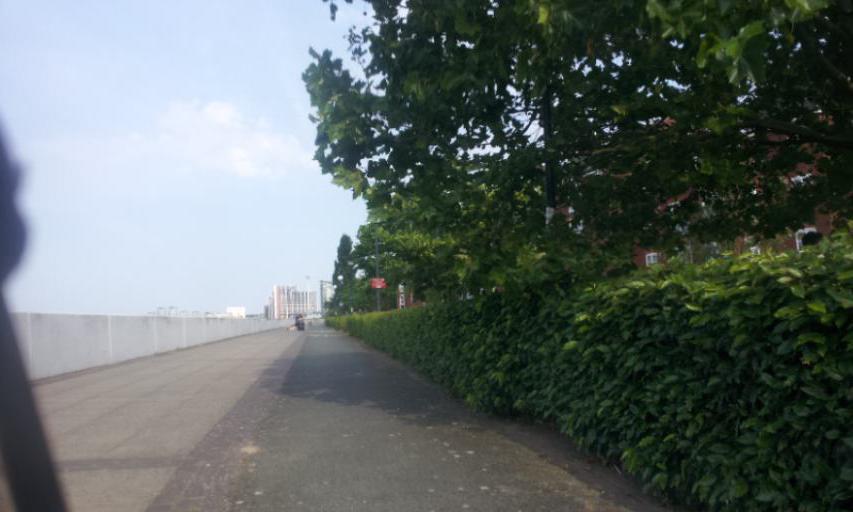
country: GB
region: England
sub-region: Greater London
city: Woolwich
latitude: 51.4950
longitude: 0.0478
